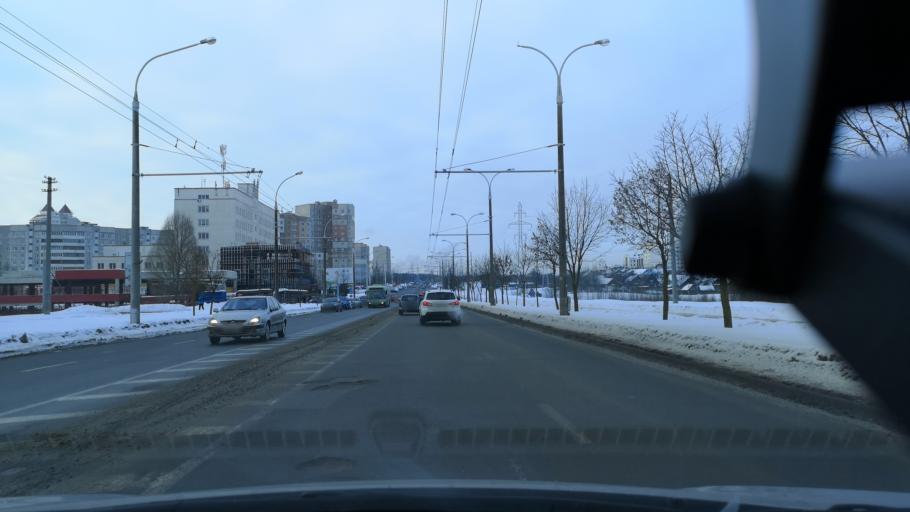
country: BY
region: Minsk
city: Borovlyany
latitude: 53.9520
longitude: 27.6798
